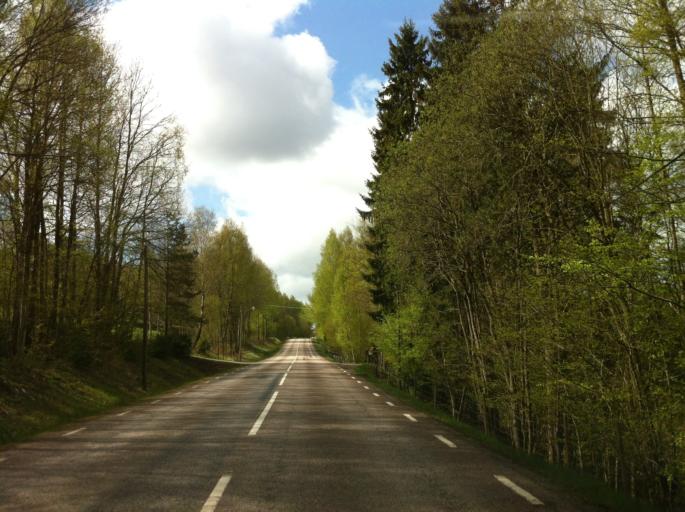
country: SE
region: Vaestra Goetaland
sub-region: Alingsas Kommun
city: Ingared
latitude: 57.8512
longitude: 12.5311
